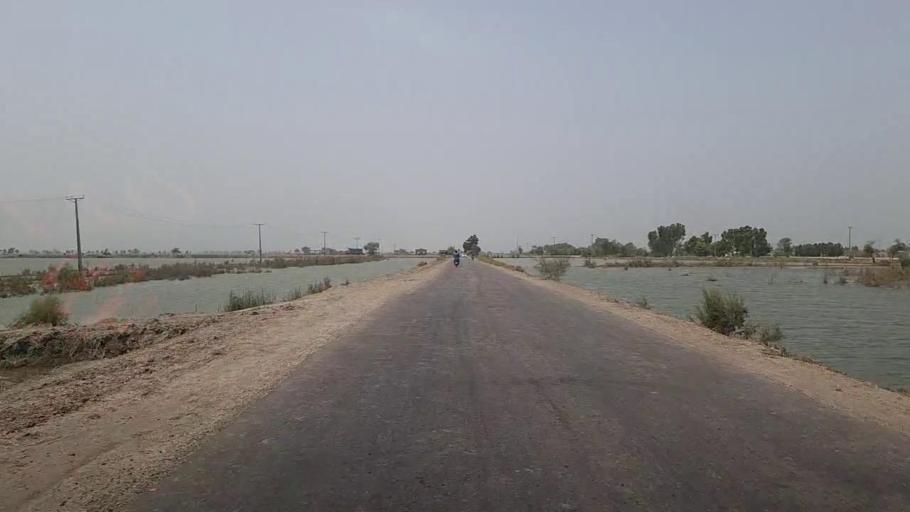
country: PK
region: Sindh
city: Radhan
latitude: 27.1475
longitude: 67.9372
